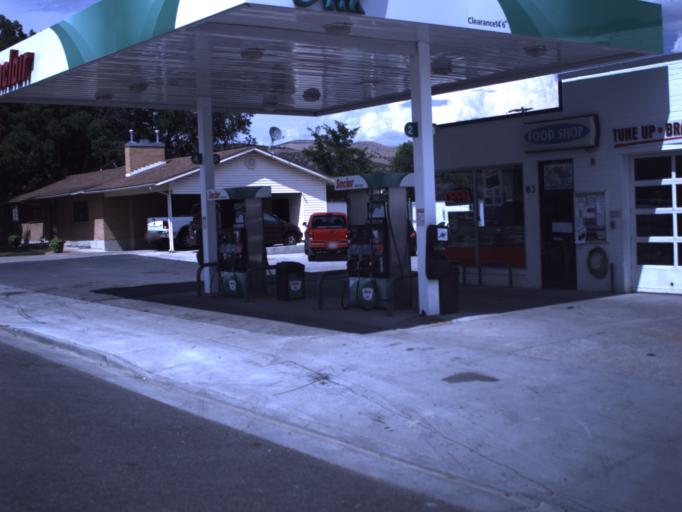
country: US
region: Utah
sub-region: Sanpete County
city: Fountain Green
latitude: 39.6271
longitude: -111.6344
